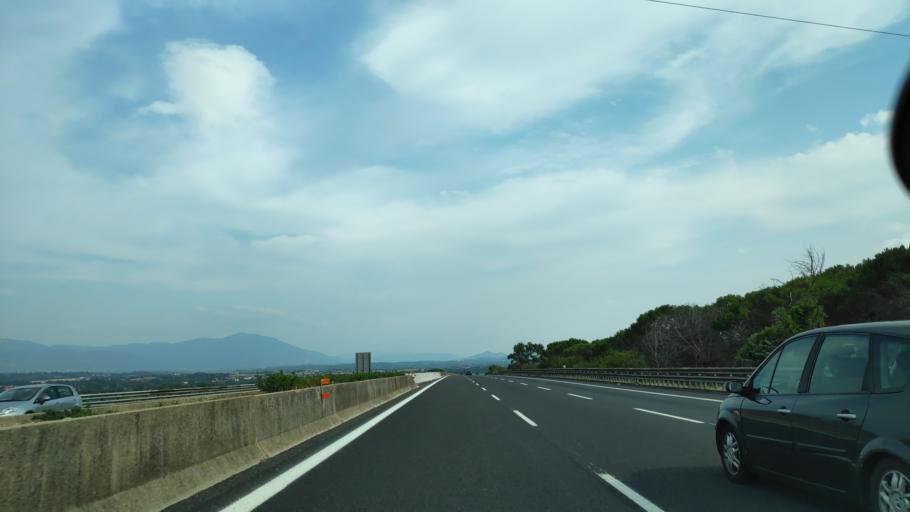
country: IT
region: Latium
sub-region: Citta metropolitana di Roma Capitale
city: Fiano Romano
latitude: 42.1627
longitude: 12.6186
